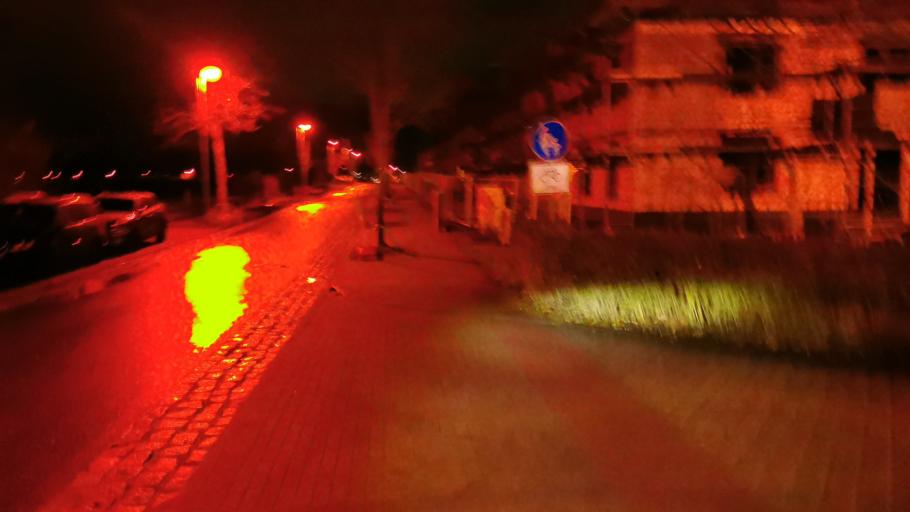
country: DE
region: Brandenburg
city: Schoneiche
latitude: 52.4799
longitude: 13.7059
